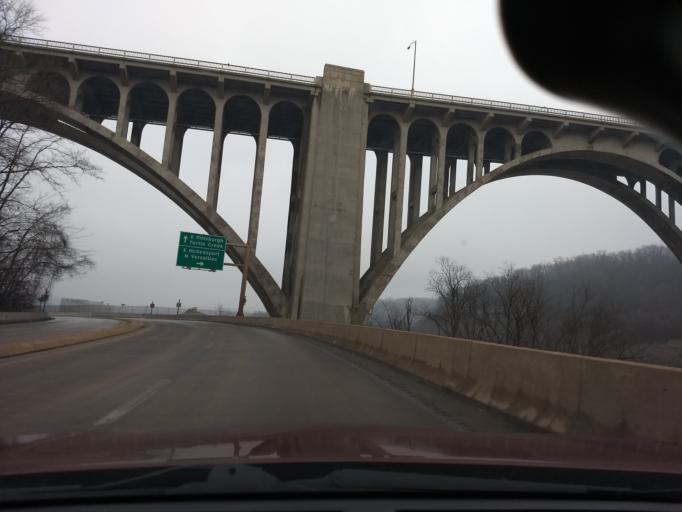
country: US
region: Pennsylvania
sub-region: Allegheny County
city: East Pittsburgh
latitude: 40.3927
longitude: -79.8375
